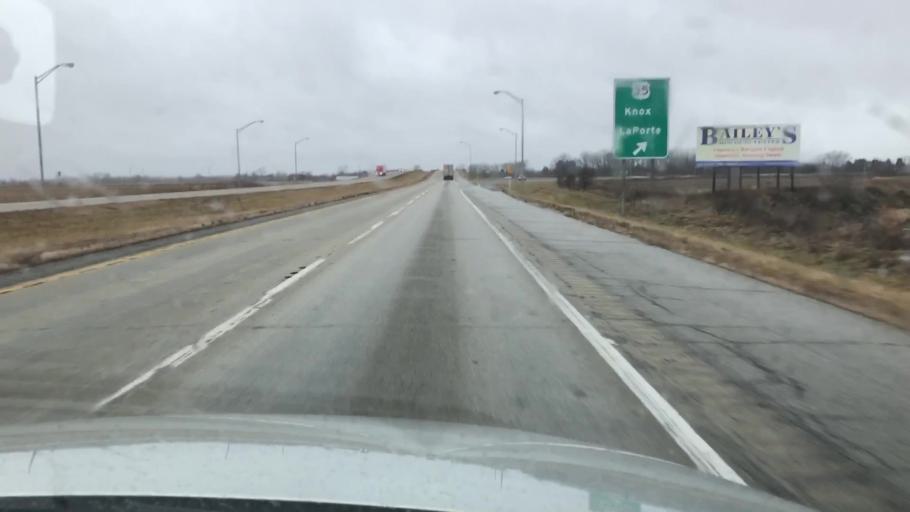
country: US
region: Indiana
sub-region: Starke County
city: Knox
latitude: 41.3940
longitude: -86.6139
